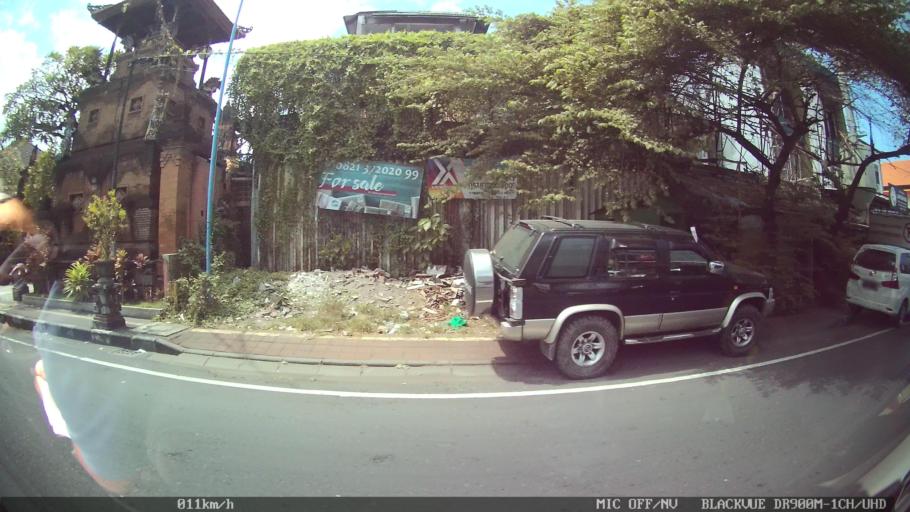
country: ID
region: Bali
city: Denpasar
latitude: -8.6652
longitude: 115.2072
